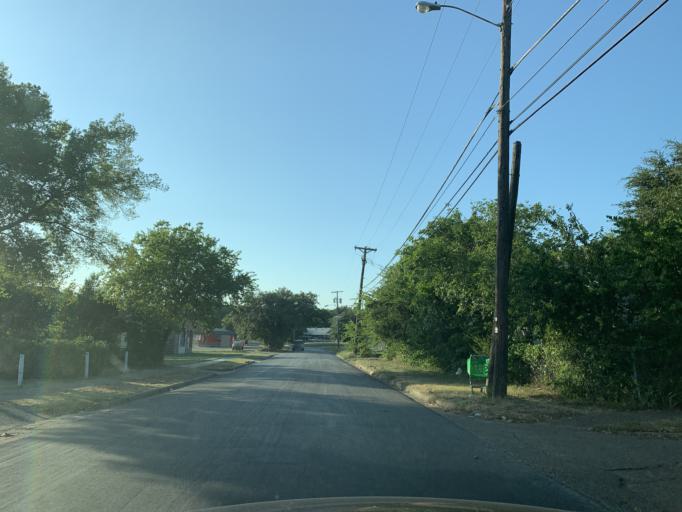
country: US
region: Texas
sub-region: Dallas County
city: Dallas
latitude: 32.7097
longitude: -96.7988
